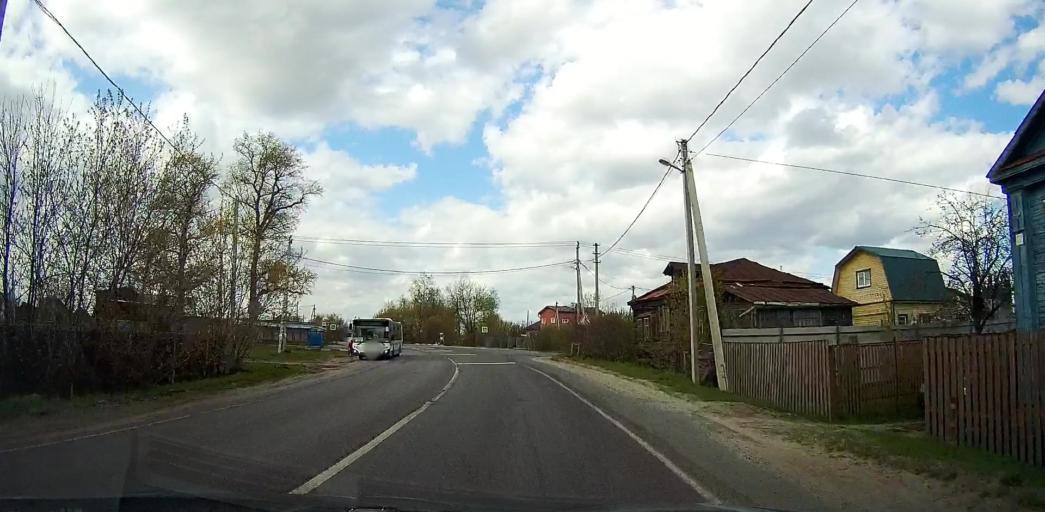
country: RU
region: Moskovskaya
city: Davydovo
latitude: 55.6361
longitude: 38.8686
